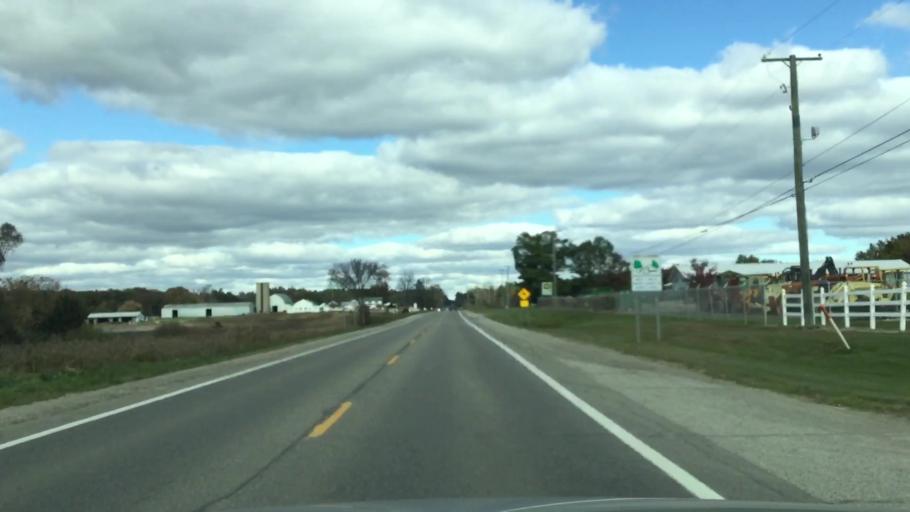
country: US
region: Michigan
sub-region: Lapeer County
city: Barnes Lake-Millers Lake
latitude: 43.1176
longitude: -83.3093
